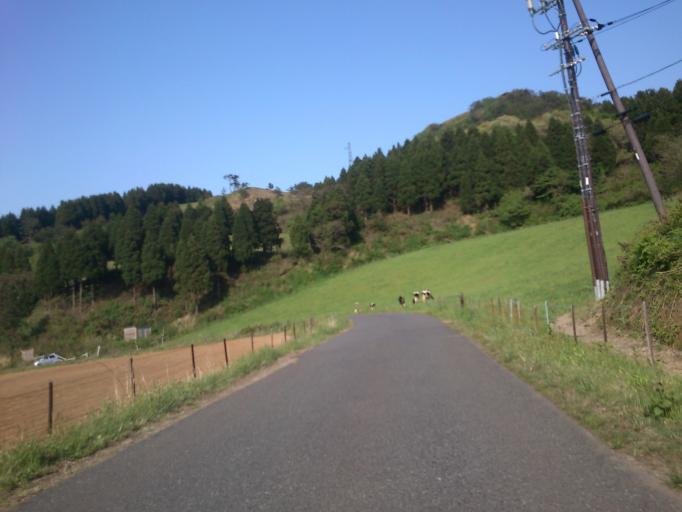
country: JP
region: Kyoto
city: Miyazu
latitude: 35.7228
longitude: 135.1952
